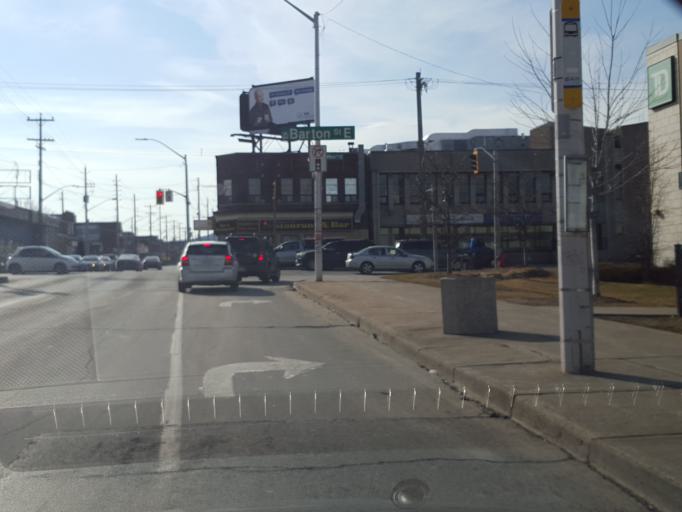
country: CA
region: Ontario
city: Hamilton
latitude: 43.2497
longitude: -79.8061
